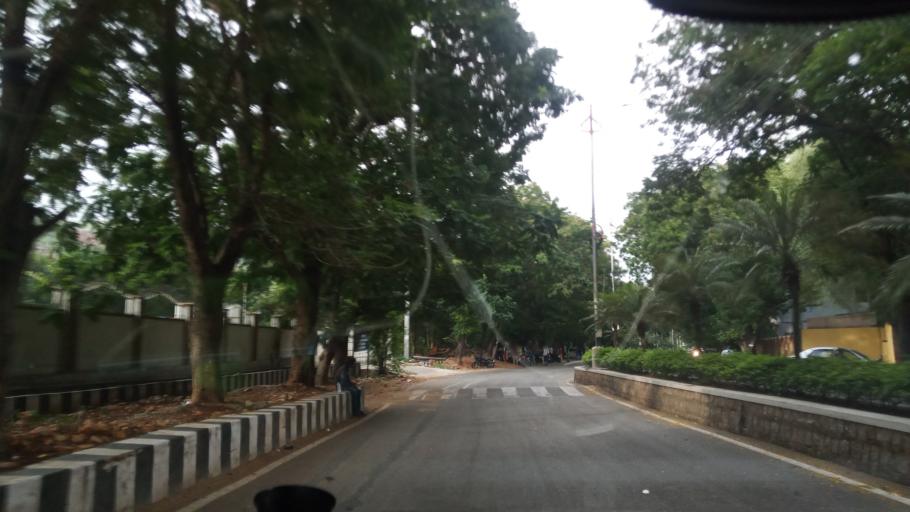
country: IN
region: Andhra Pradesh
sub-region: Chittoor
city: Akkarampalle
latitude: 13.6464
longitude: 79.4110
